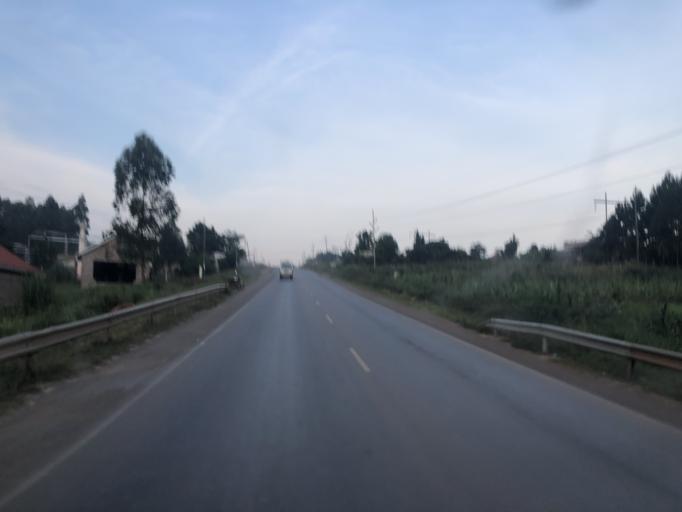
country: UG
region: Central Region
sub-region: Mpigi District
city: Mpigi
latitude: 0.2424
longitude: 32.3620
